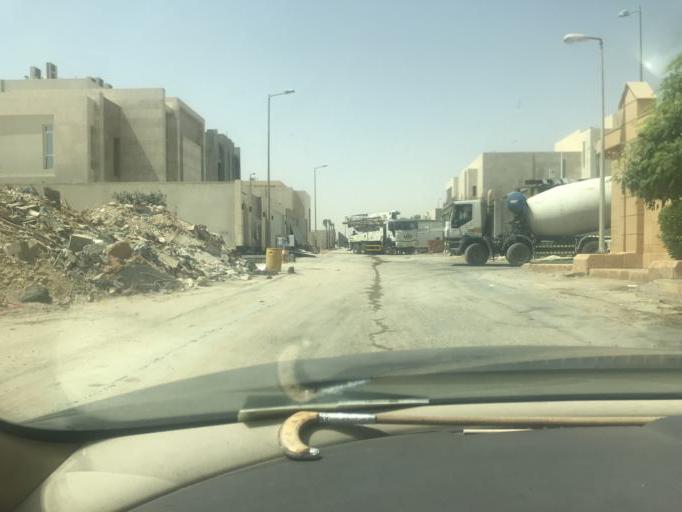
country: SA
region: Ar Riyad
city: Riyadh
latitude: 24.7860
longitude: 46.5825
